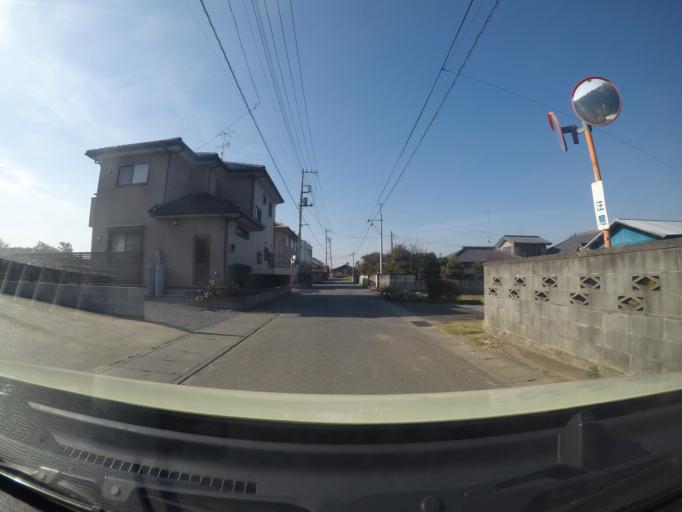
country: JP
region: Ibaraki
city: Tsukuba
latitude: 36.1919
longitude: 140.0916
